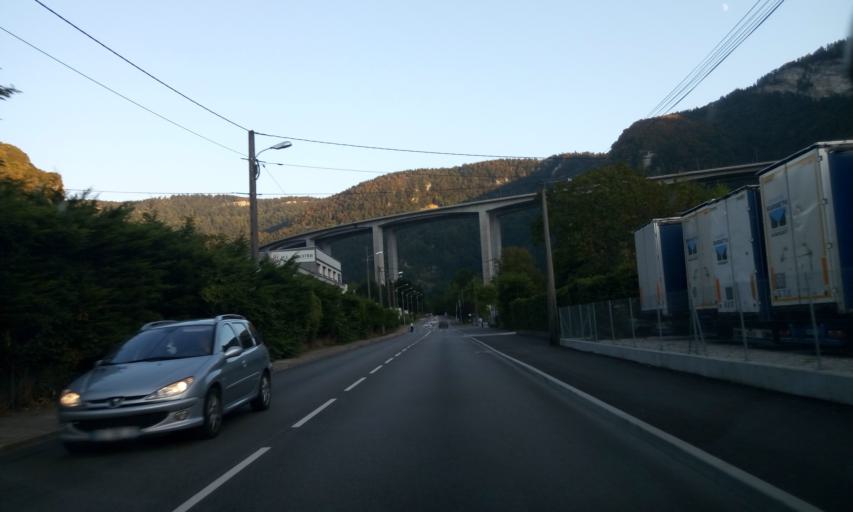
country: FR
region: Rhone-Alpes
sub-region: Departement de l'Ain
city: Nantua
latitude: 46.1459
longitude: 5.6126
